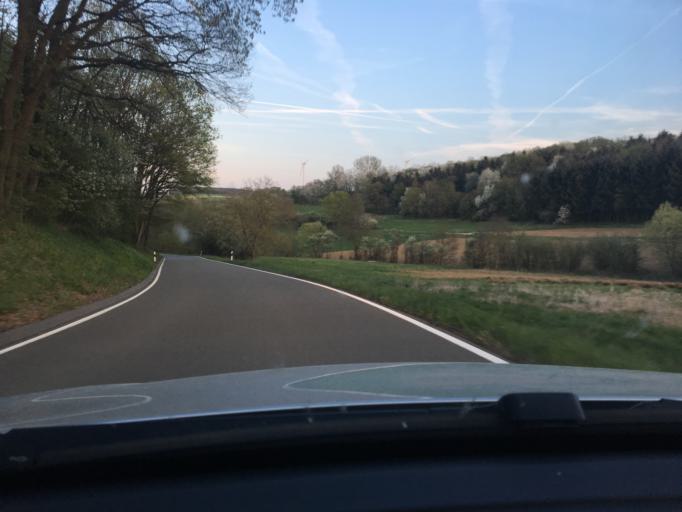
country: DE
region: Rheinland-Pfalz
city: Winterborn
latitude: 49.7445
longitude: 7.8743
